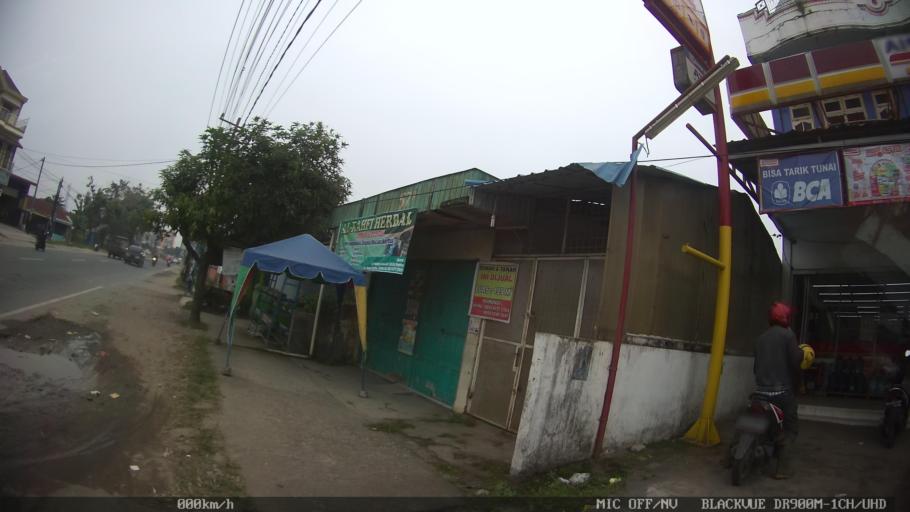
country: ID
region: North Sumatra
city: Deli Tua
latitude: 3.5471
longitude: 98.7171
